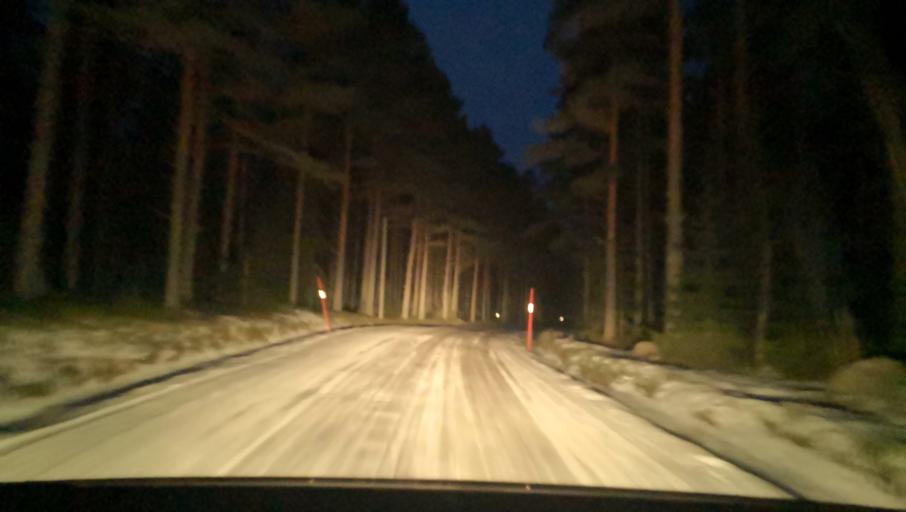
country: SE
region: Uppsala
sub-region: Heby Kommun
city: Tarnsjo
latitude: 60.2763
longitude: 16.8000
